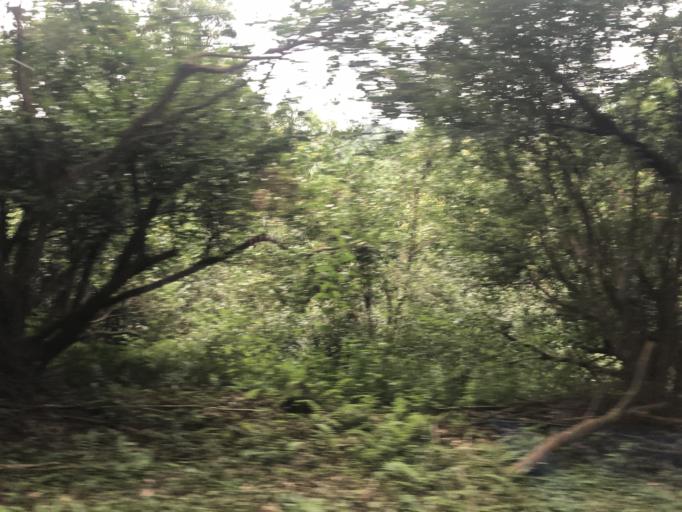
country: TW
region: Taiwan
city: Daxi
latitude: 24.8819
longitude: 121.4185
